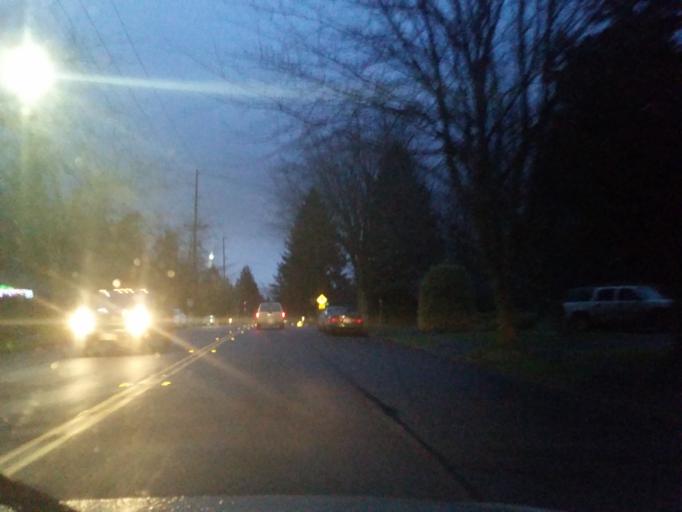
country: US
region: Washington
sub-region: King County
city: Shoreline
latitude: 47.7535
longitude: -122.3240
